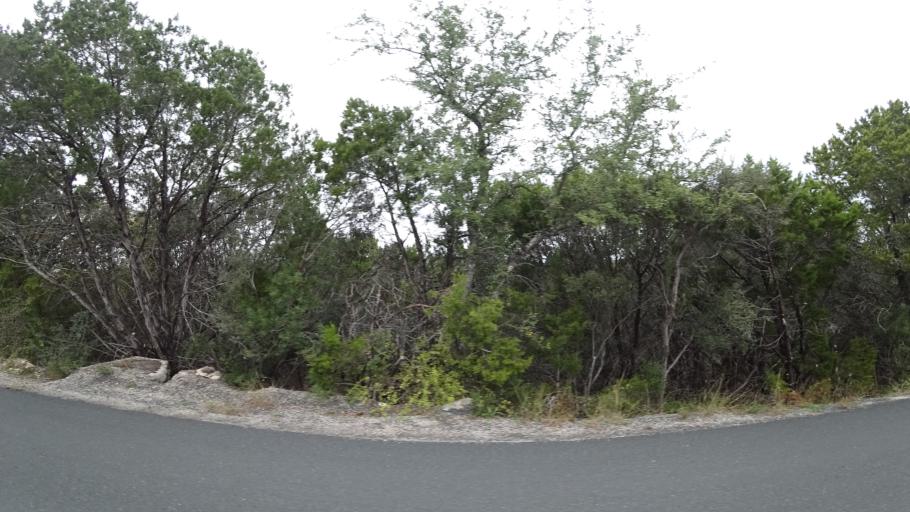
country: US
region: Texas
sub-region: Travis County
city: Bee Cave
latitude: 30.3504
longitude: -97.9354
